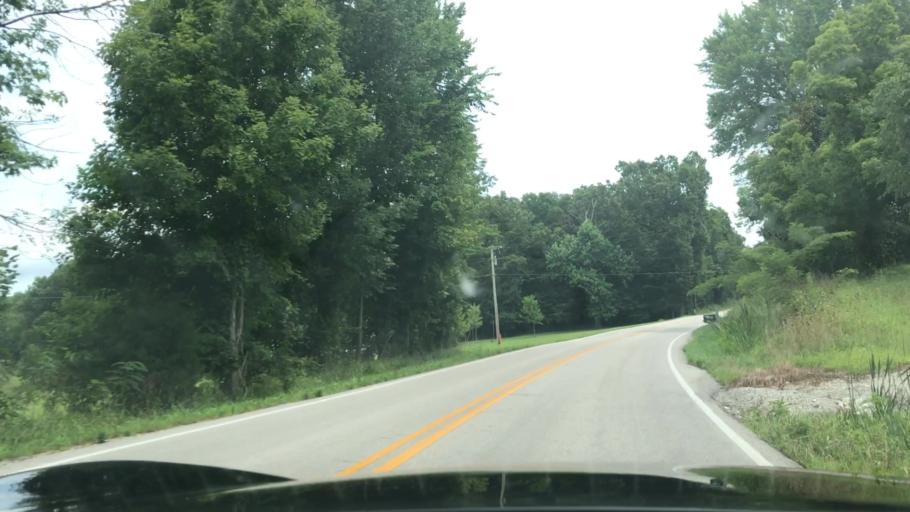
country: US
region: Kentucky
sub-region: Butler County
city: Morgantown
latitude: 37.1746
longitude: -86.8390
